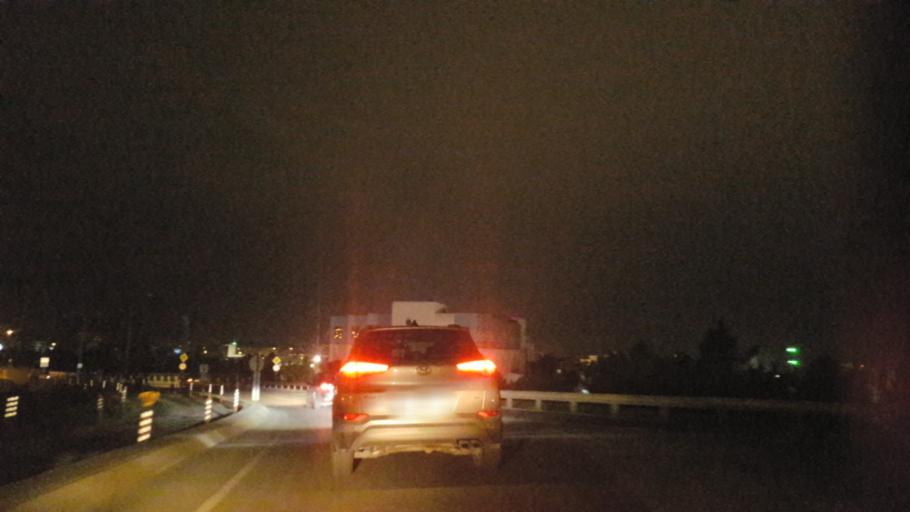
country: TR
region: Istanbul
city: Icmeler
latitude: 40.8339
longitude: 29.3258
